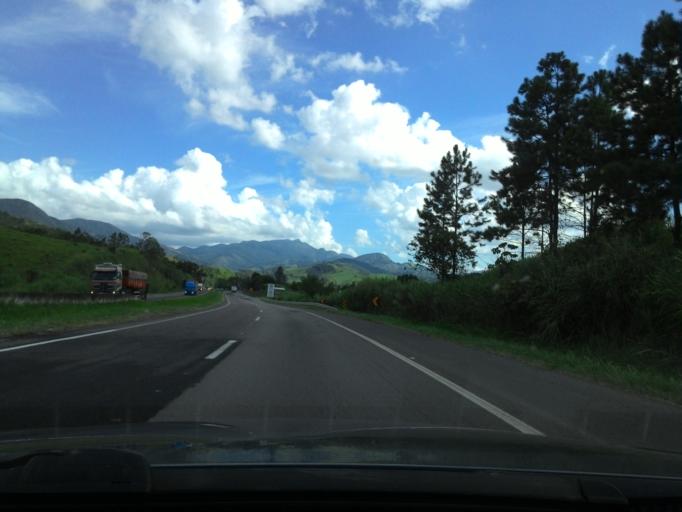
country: BR
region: Sao Paulo
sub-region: Cajati
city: Cajati
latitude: -24.7699
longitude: -48.1704
